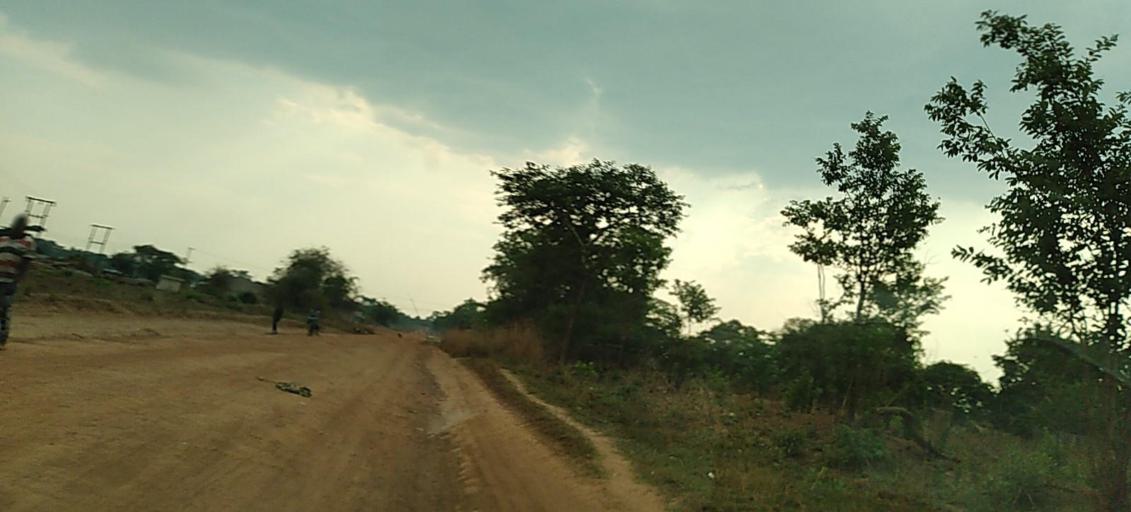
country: ZM
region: Copperbelt
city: Kalulushi
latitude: -12.9516
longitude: 27.9090
